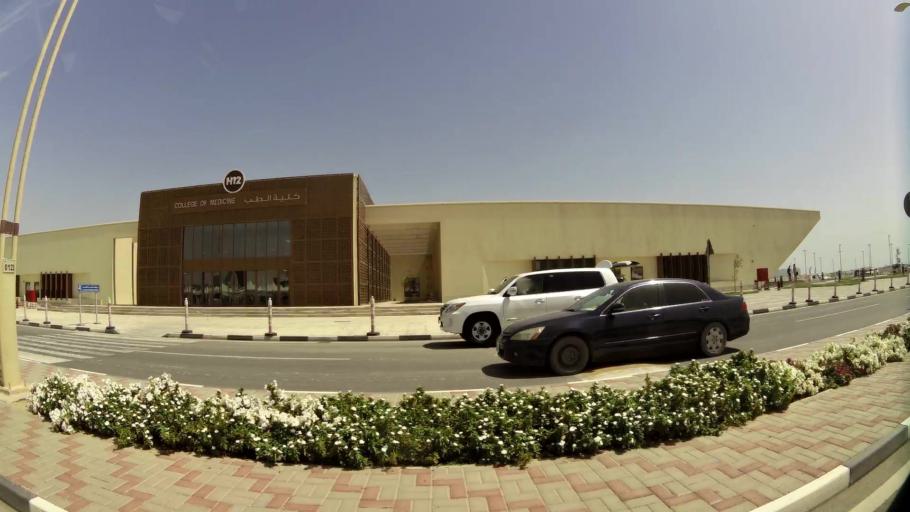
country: QA
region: Baladiyat Umm Salal
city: Umm Salal Muhammad
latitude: 25.3800
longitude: 51.4920
